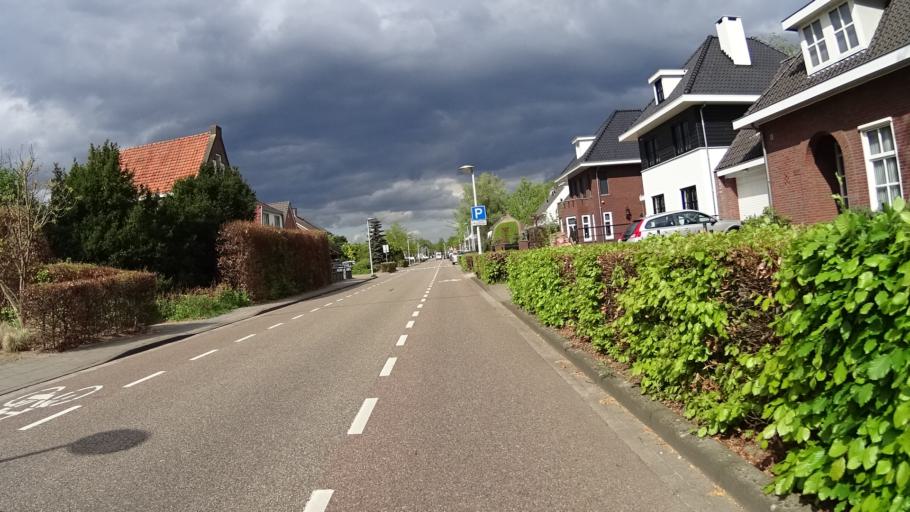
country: NL
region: North Brabant
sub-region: Gemeente Nuenen, Gerwen en Nederwetten
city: Nuenen
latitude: 51.4640
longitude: 5.5371
